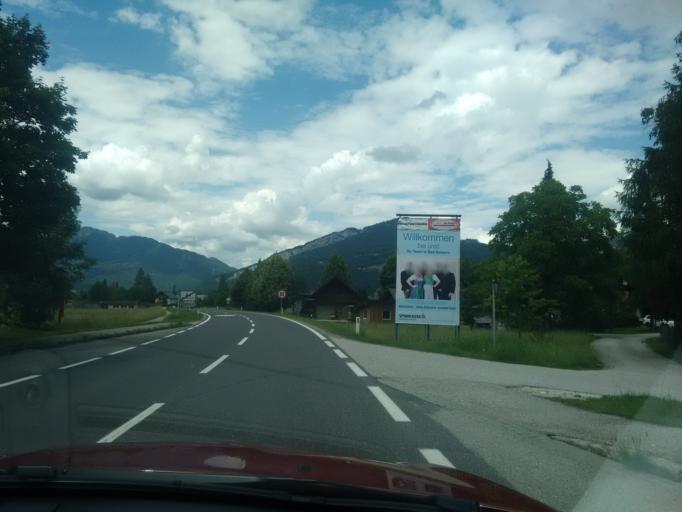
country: AT
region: Upper Austria
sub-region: Politischer Bezirk Gmunden
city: Bad Goisern
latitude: 47.6181
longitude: 13.6350
